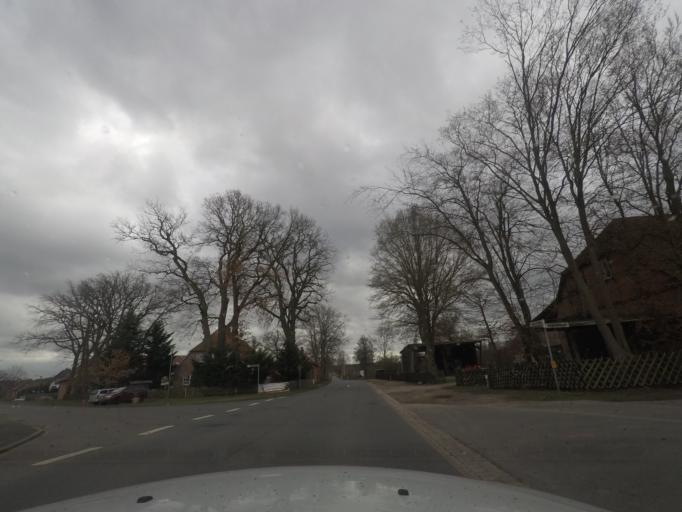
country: DE
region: Lower Saxony
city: Bad Bevensen
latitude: 53.0439
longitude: 10.6029
